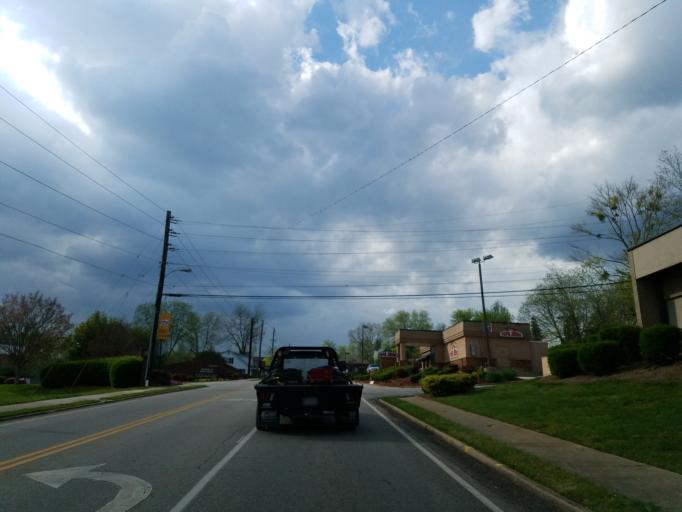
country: US
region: Georgia
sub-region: Lumpkin County
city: Dahlonega
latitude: 34.5285
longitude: -83.9812
